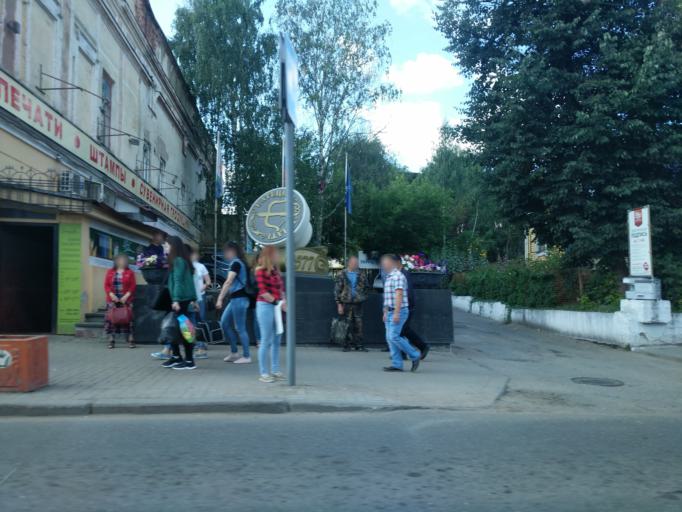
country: RU
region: Kirov
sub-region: Kirovo-Chepetskiy Rayon
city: Kirov
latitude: 58.6050
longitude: 49.6807
